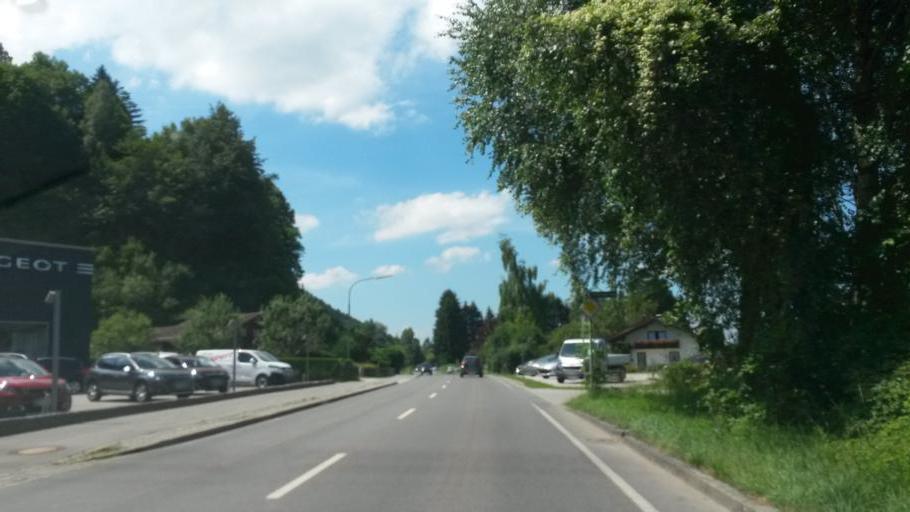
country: DE
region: Bavaria
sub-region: Upper Bavaria
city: Grassau
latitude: 47.7783
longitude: 12.4421
